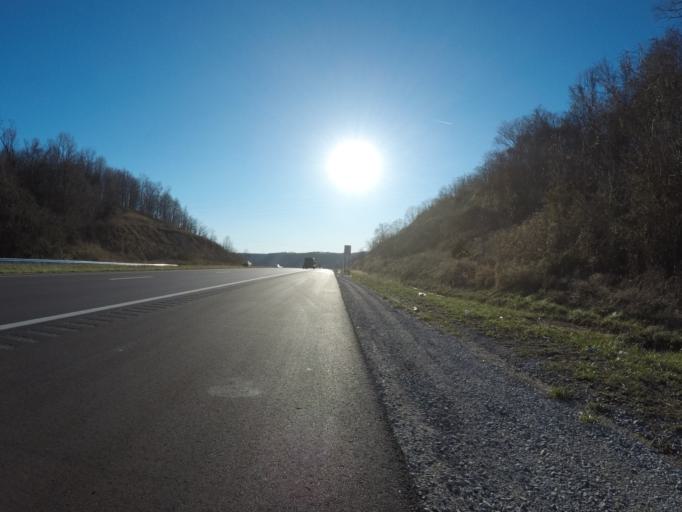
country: US
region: West Virginia
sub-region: Wayne County
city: Kenova
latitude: 38.3790
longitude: -82.5840
